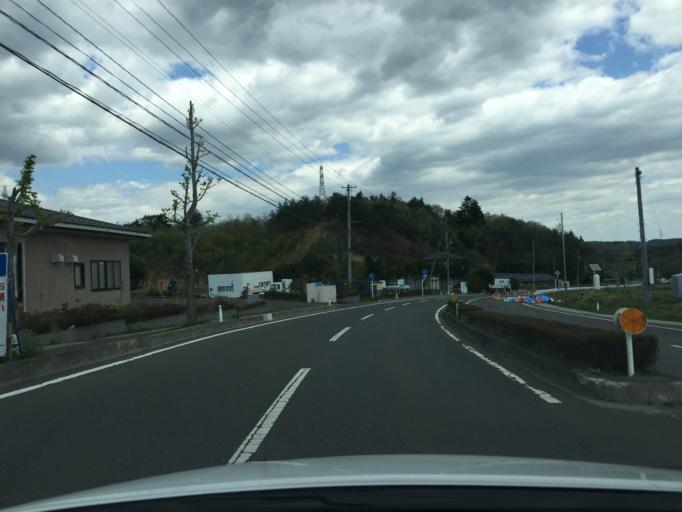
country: JP
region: Fukushima
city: Yanagawamachi-saiwaicho
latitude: 37.6811
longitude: 140.7369
